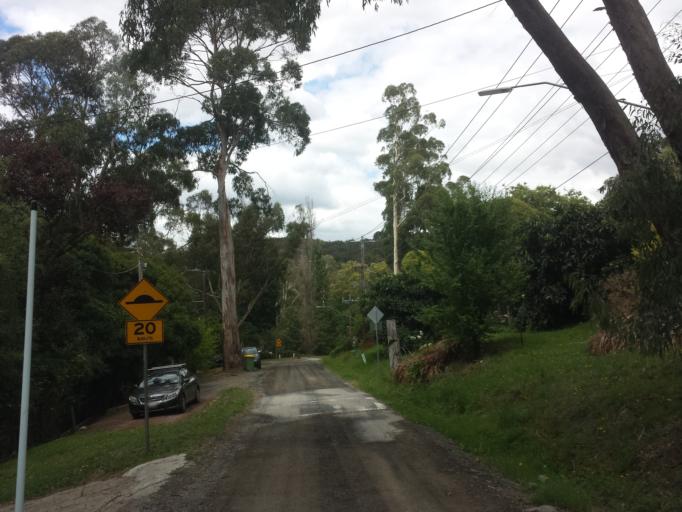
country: AU
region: Victoria
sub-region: Yarra Ranges
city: Belgrave Heights
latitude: -37.9195
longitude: 145.3563
